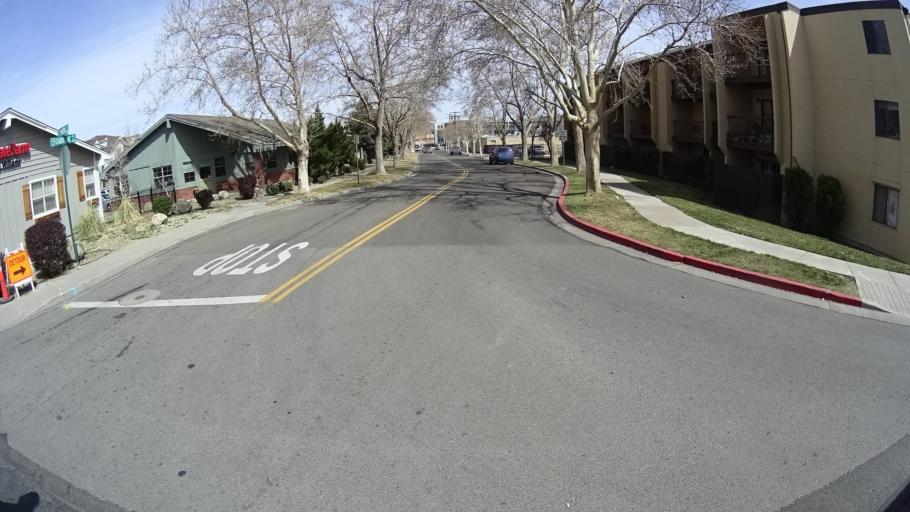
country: US
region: Nevada
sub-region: Washoe County
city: Reno
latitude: 39.5009
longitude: -119.8037
